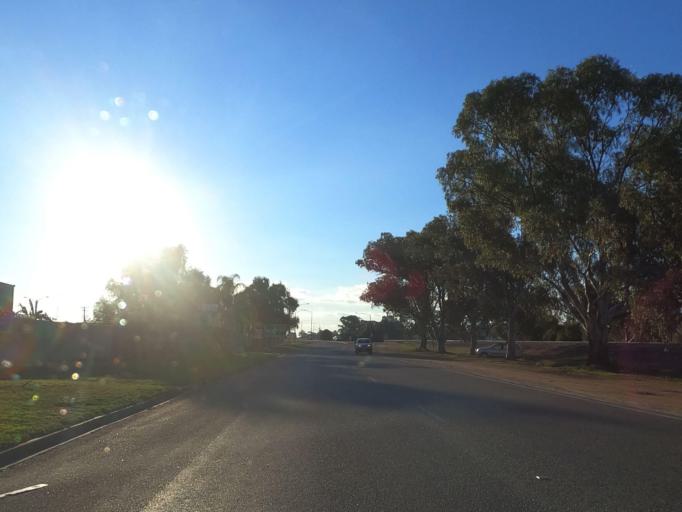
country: AU
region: Victoria
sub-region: Swan Hill
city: Swan Hill
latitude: -35.3291
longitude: 143.5551
